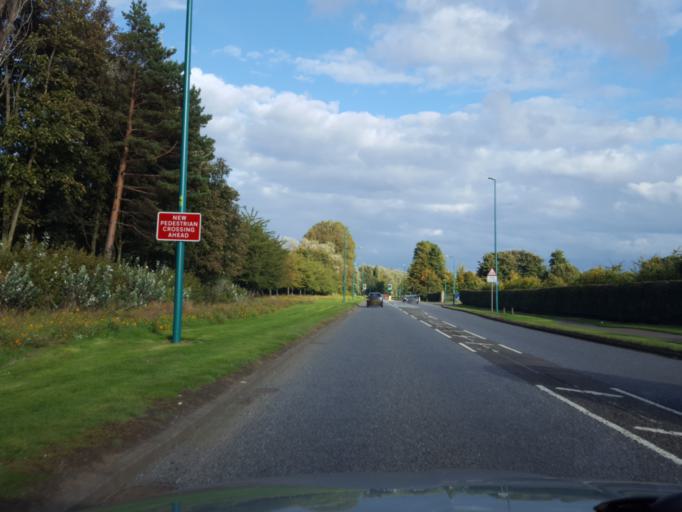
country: GB
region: Scotland
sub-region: Dundee City
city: Dundee
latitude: 56.4544
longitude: -3.0117
